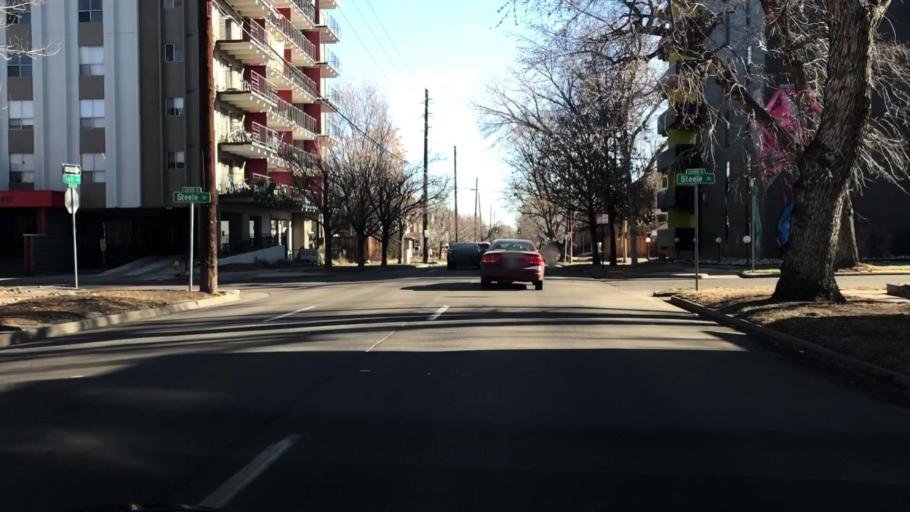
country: US
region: Colorado
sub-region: Denver County
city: Denver
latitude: 39.7383
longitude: -104.9498
